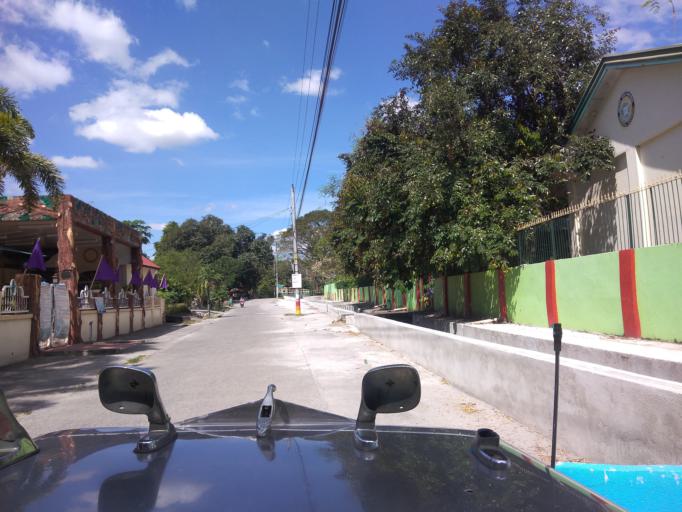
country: PH
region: Central Luzon
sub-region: Province of Pampanga
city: Santa Rita
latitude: 15.0068
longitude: 120.5929
